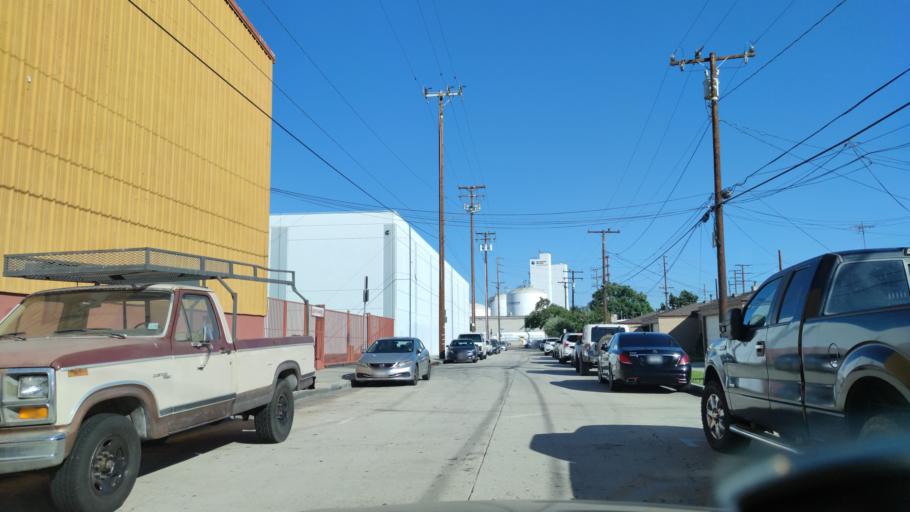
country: US
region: California
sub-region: Los Angeles County
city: Maywood
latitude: 33.9907
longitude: -118.1793
